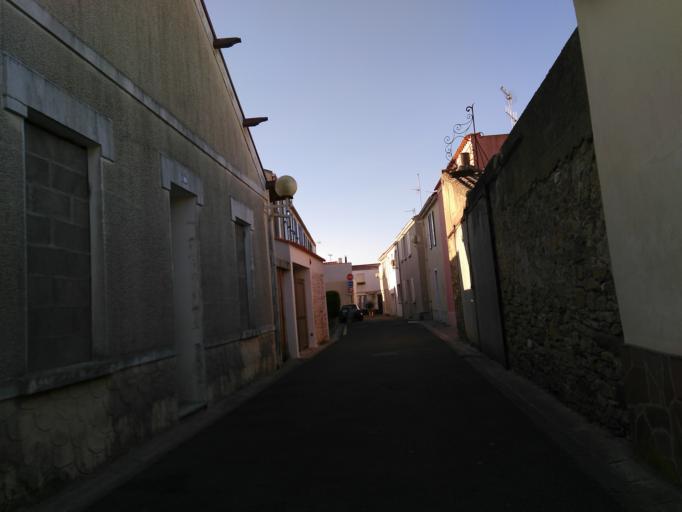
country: FR
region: Pays de la Loire
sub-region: Departement de la Vendee
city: Les Sables-d'Olonne
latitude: 46.4967
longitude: -1.7982
